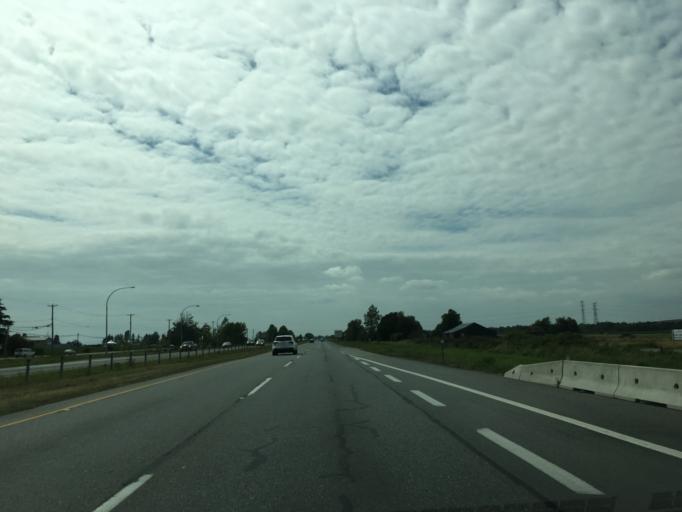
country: CA
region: British Columbia
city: Delta
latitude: 49.0906
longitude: -122.9663
